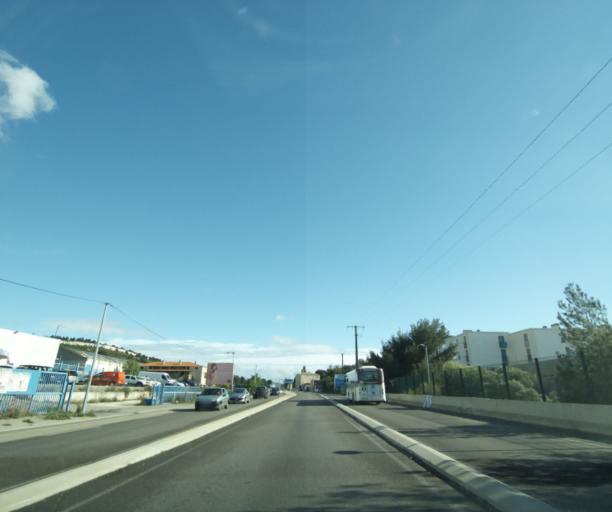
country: FR
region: Provence-Alpes-Cote d'Azur
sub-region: Departement des Bouches-du-Rhone
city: Vitrolles
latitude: 43.4627
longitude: 5.2321
